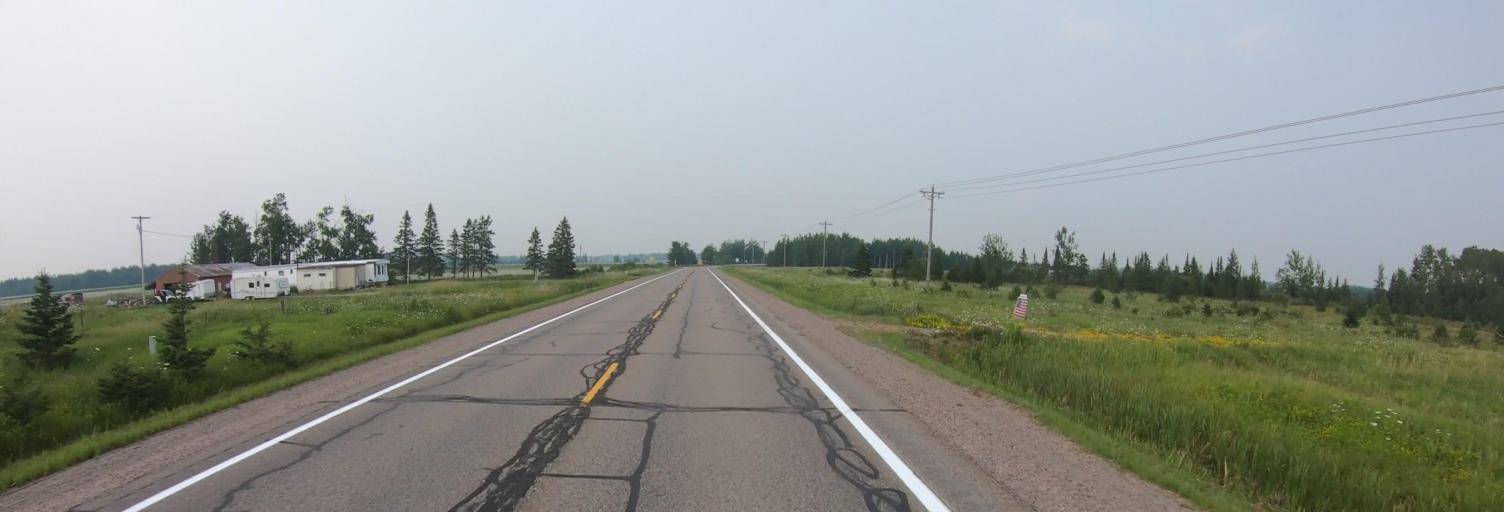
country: US
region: Michigan
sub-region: Chippewa County
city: Sault Ste. Marie
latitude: 46.3636
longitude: -84.3640
